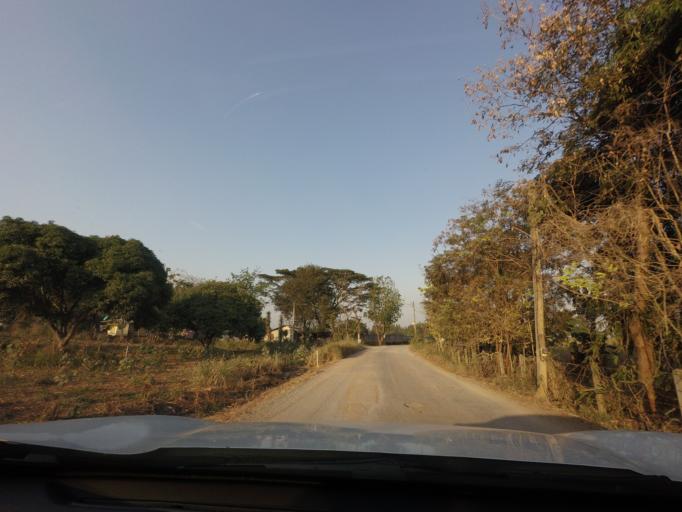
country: TH
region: Nakhon Ratchasima
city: Pak Chong
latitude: 14.6419
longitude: 101.3701
